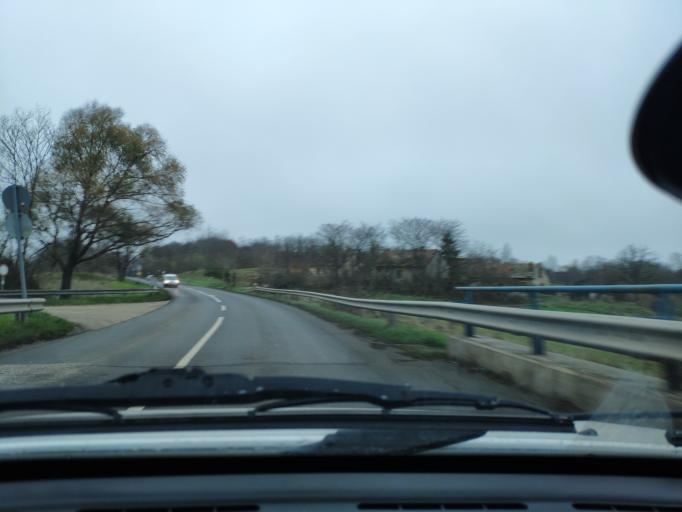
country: HU
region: Pest
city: Biatorbagy
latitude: 47.4507
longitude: 18.8229
